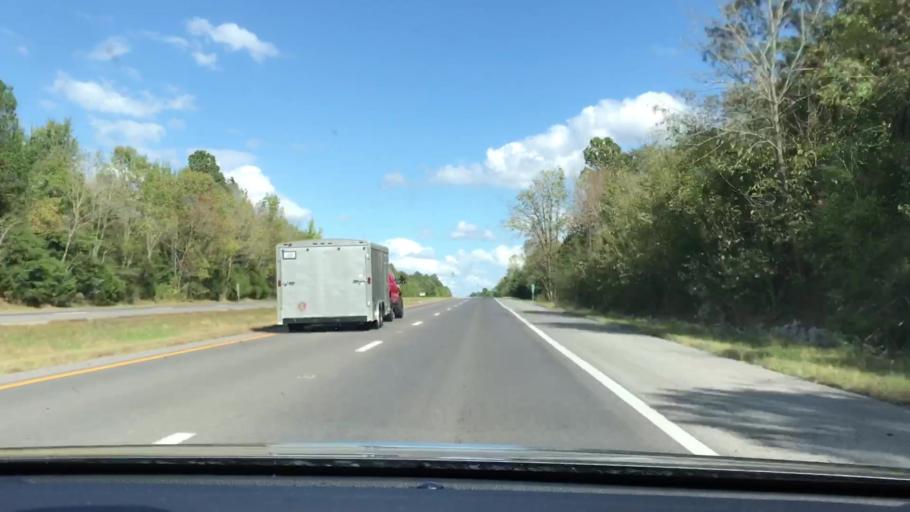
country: US
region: Kentucky
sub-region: Marshall County
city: Benton
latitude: 36.8369
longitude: -88.4283
